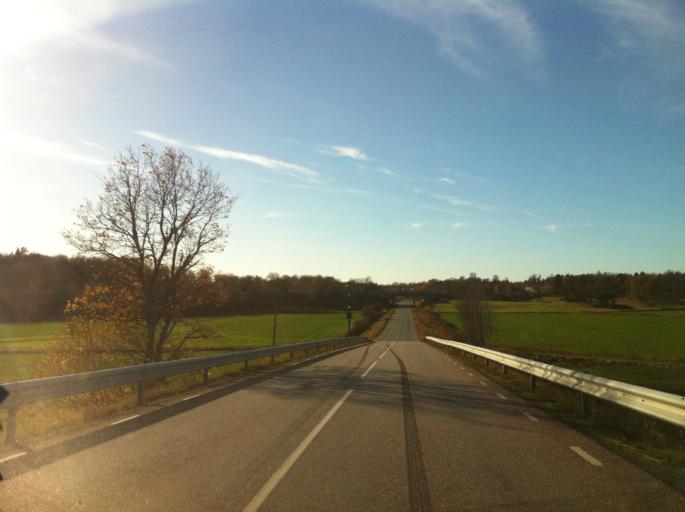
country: SE
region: Blekinge
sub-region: Ronneby Kommun
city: Brakne-Hoby
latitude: 56.2104
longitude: 15.0605
